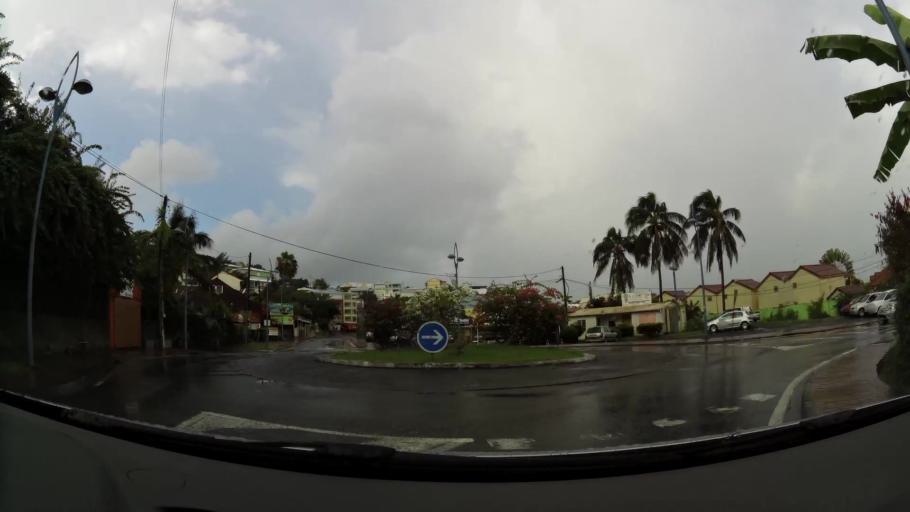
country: MQ
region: Martinique
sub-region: Martinique
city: Les Trois-Ilets
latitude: 14.5504
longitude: -61.0522
